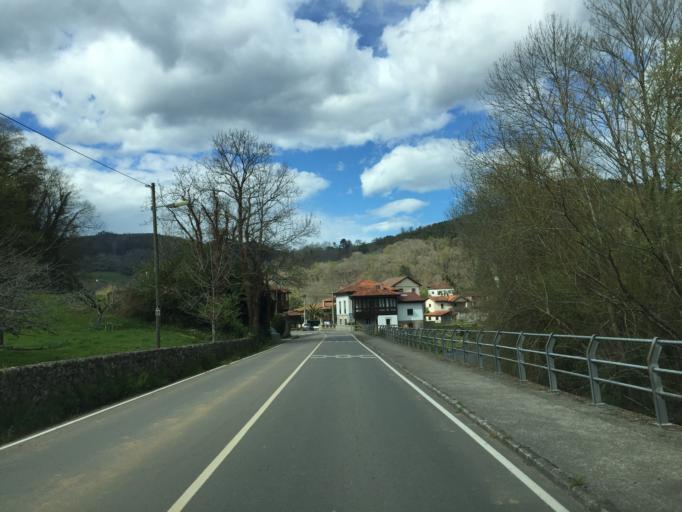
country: ES
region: Asturias
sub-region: Province of Asturias
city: Cangas de Onis
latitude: 43.3430
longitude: -5.0838
